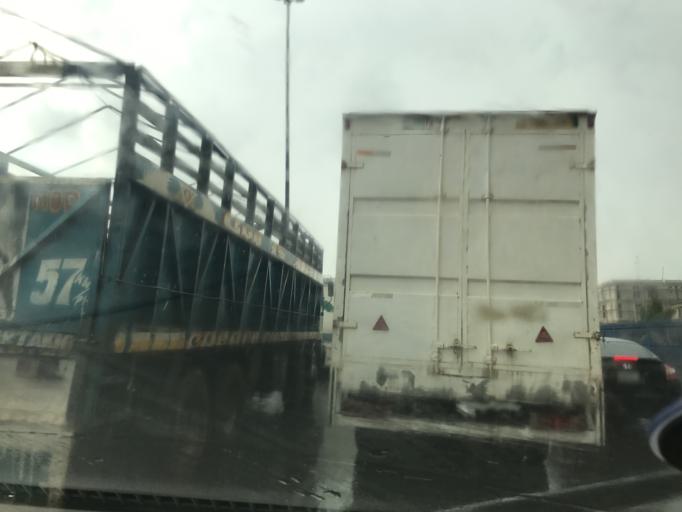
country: NG
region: Lagos
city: Oshodi
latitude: 6.5544
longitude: 3.3483
